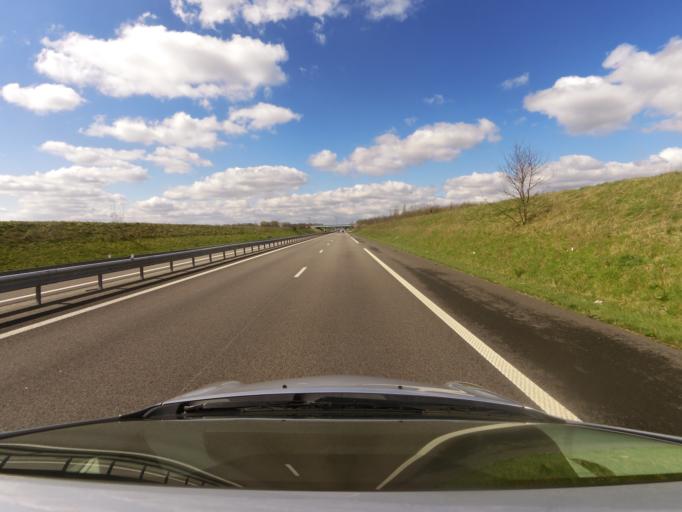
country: FR
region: Haute-Normandie
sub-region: Departement de la Seine-Maritime
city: Cleres
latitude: 49.6380
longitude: 1.0832
